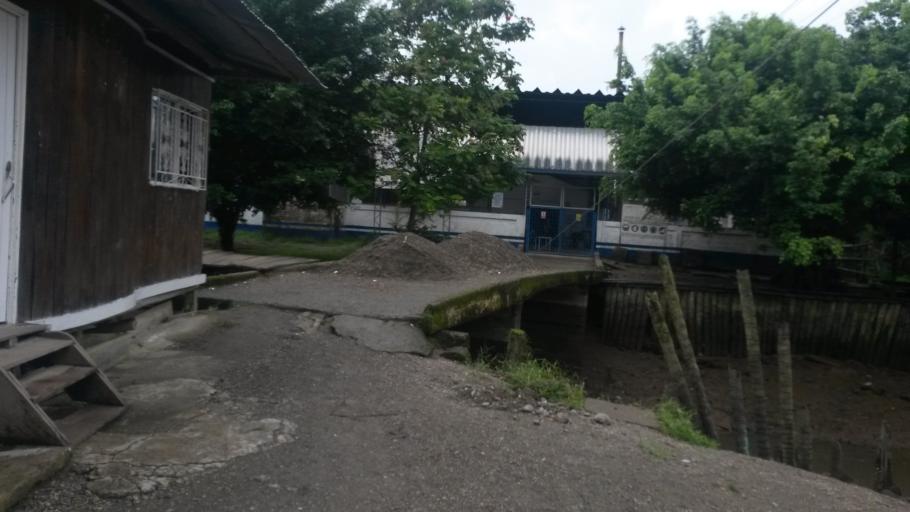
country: CO
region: Cauca
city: Guapi
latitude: 2.5679
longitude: -77.8842
